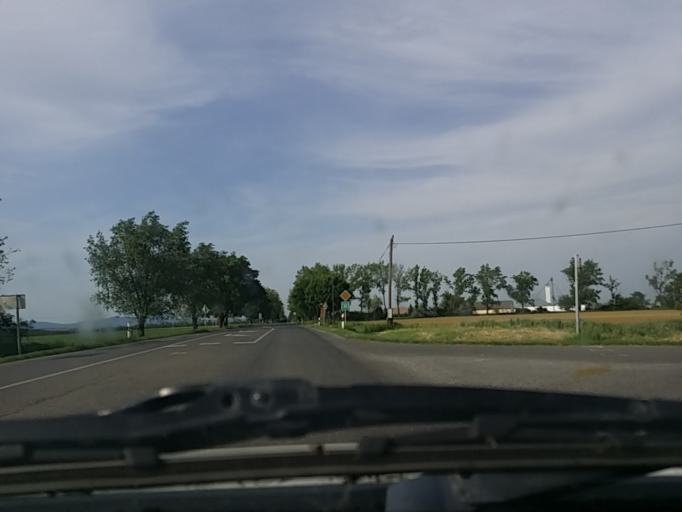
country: HU
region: Baranya
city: Harkany
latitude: 45.9178
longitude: 18.2328
